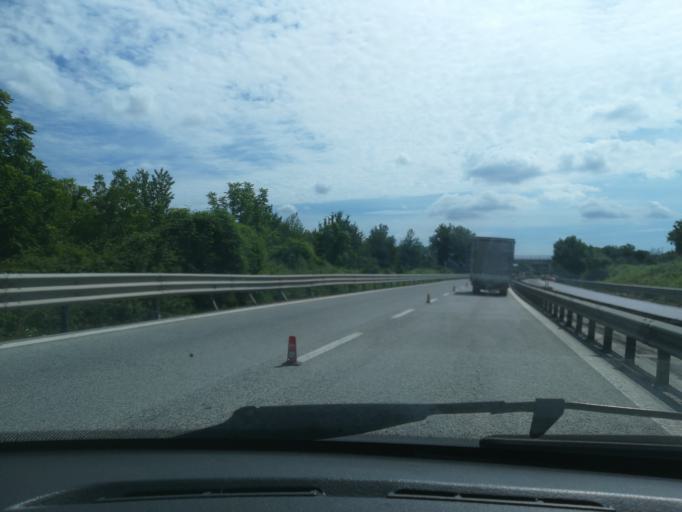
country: IT
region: The Marches
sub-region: Provincia di Macerata
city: Zona Industriale
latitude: 43.2693
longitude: 13.5036
